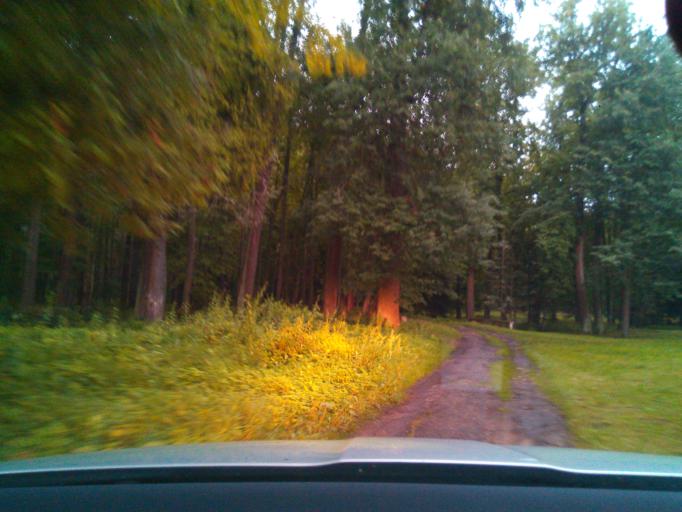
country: RU
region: Tverskaya
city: Konakovo
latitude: 56.6881
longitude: 36.6992
